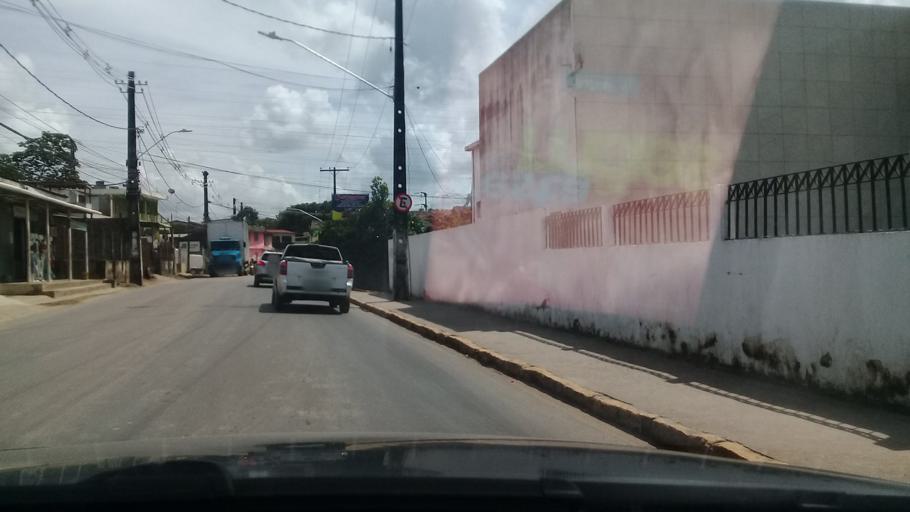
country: BR
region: Pernambuco
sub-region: Jaboatao Dos Guararapes
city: Jaboatao dos Guararapes
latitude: -8.0962
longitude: -35.0206
